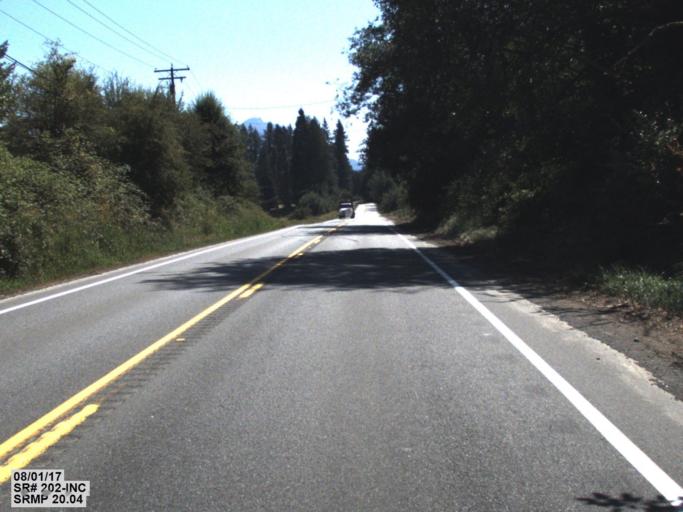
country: US
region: Washington
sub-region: King County
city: Fall City
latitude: 47.5761
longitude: -121.9200
